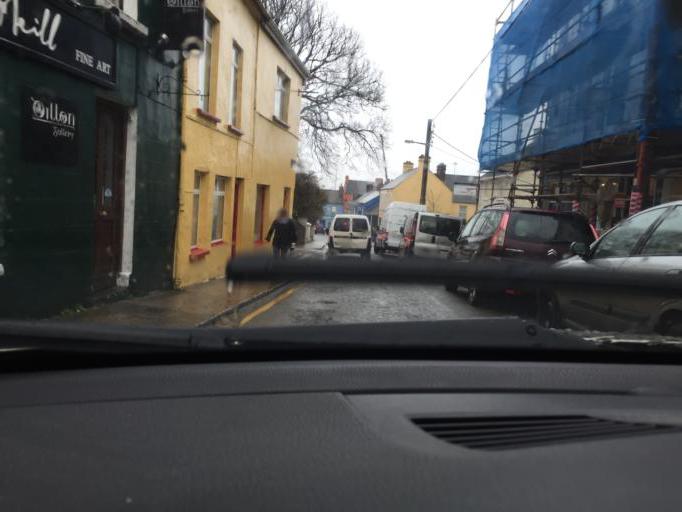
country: IE
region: Munster
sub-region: Ciarrai
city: Dingle
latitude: 52.1408
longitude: -10.2712
